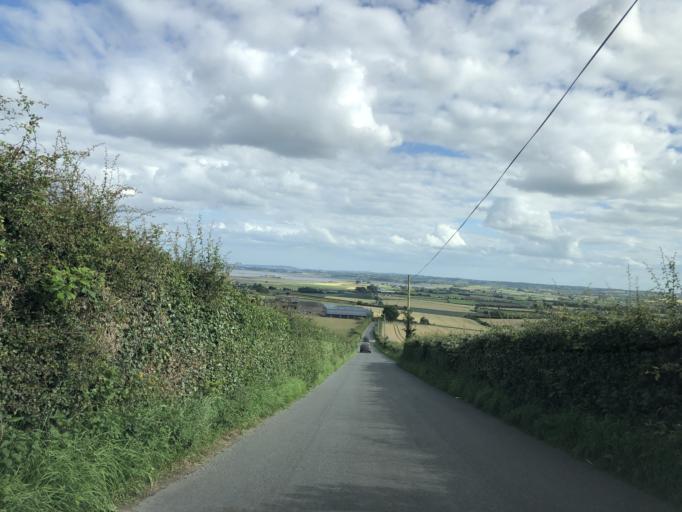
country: GB
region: Northern Ireland
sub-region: Ards District
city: Newtownards
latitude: 54.5761
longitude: -5.7172
